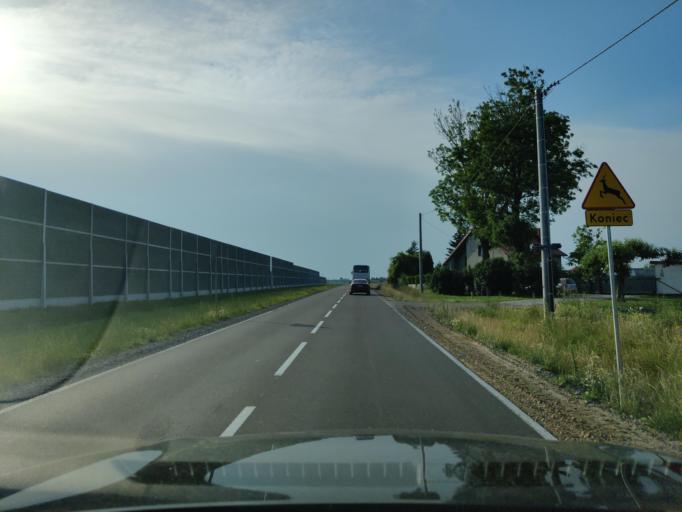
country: PL
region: Masovian Voivodeship
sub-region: Powiat plonski
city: Plonsk
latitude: 52.6896
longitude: 20.3555
